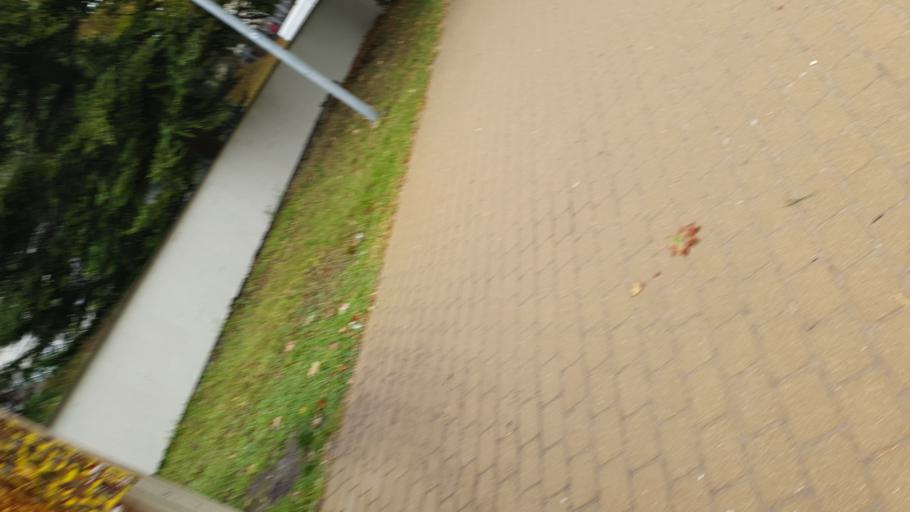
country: LV
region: Jurmala
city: Jurmala
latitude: 56.9753
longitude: 23.7983
